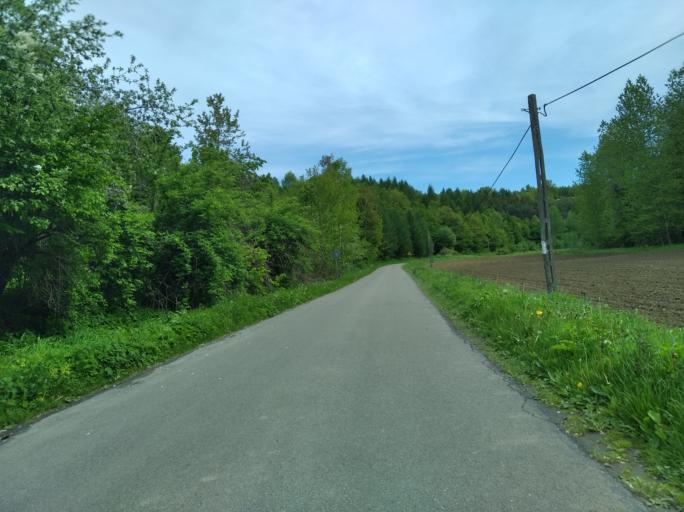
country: PL
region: Subcarpathian Voivodeship
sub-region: Powiat strzyzowski
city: Strzyzow
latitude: 49.9259
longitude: 21.7538
